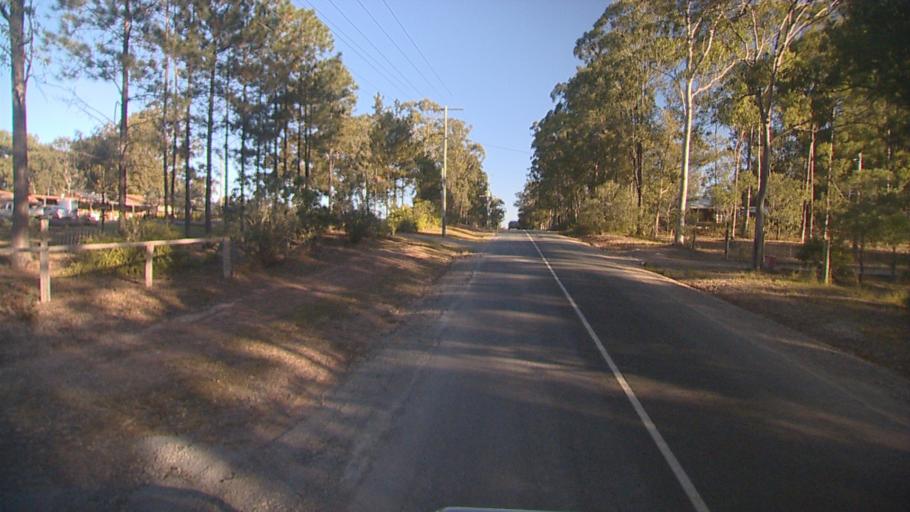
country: AU
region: Queensland
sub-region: Logan
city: Chambers Flat
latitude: -27.7767
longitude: 153.1363
